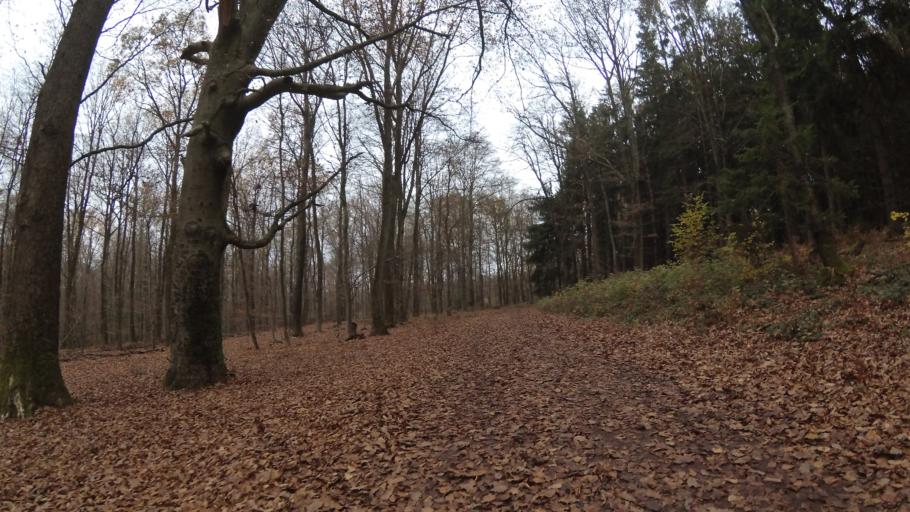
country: DE
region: Saarland
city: Mainzweiler
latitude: 49.3968
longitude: 7.1171
